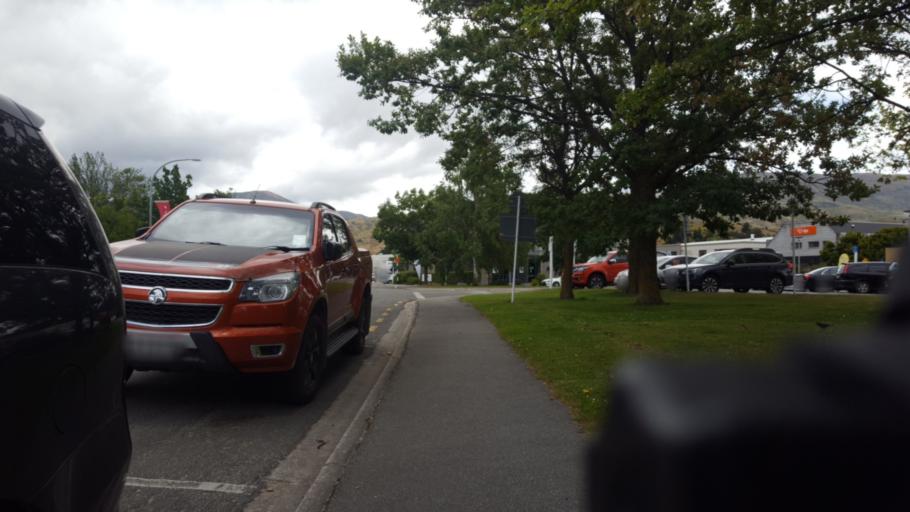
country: NZ
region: Otago
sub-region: Queenstown-Lakes District
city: Wanaka
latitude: -45.0381
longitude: 169.1973
